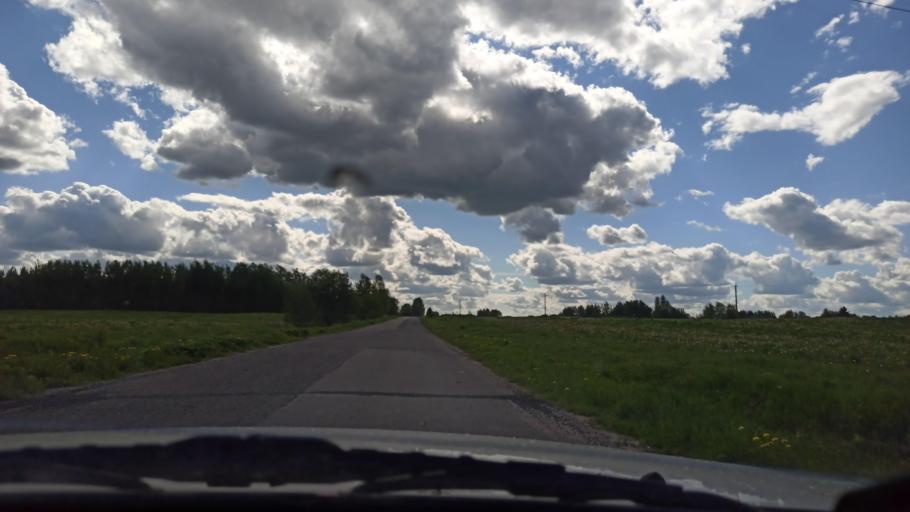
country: RU
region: Vologda
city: Molochnoye
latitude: 59.3845
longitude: 39.7309
